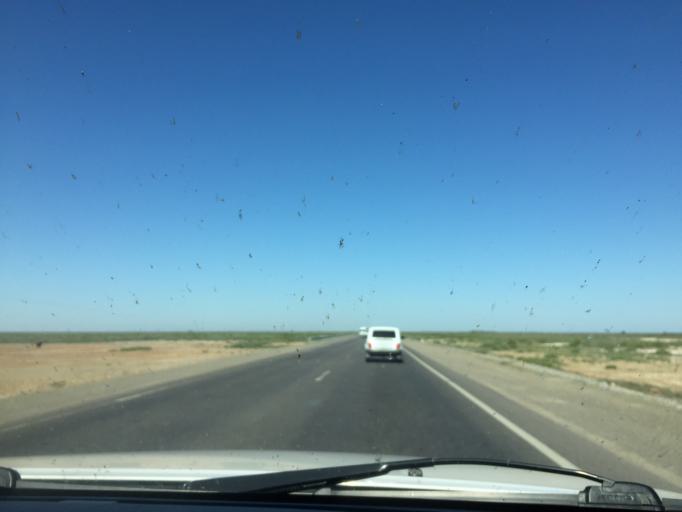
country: KZ
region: Qyzylorda
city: Kyzyl-Orda
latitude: 44.8850
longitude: 65.2594
